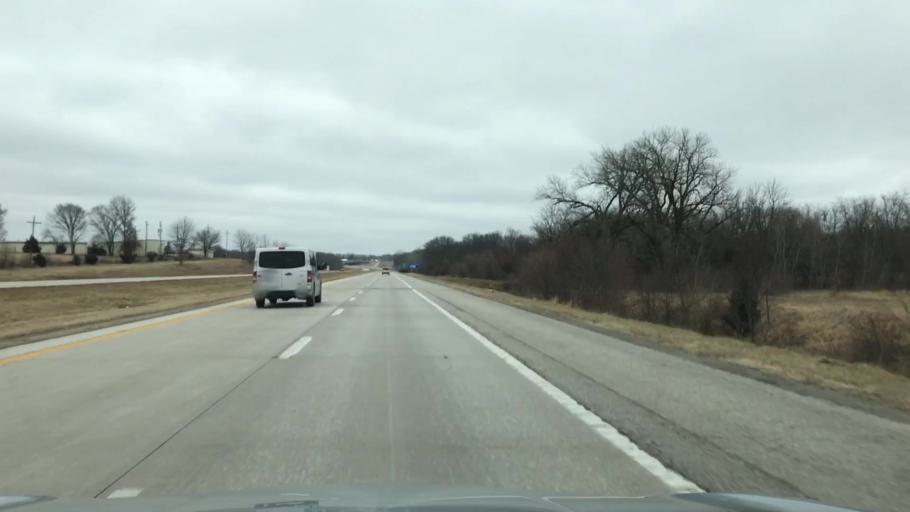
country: US
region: Missouri
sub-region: Linn County
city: Brookfield
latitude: 39.7773
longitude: -93.0953
